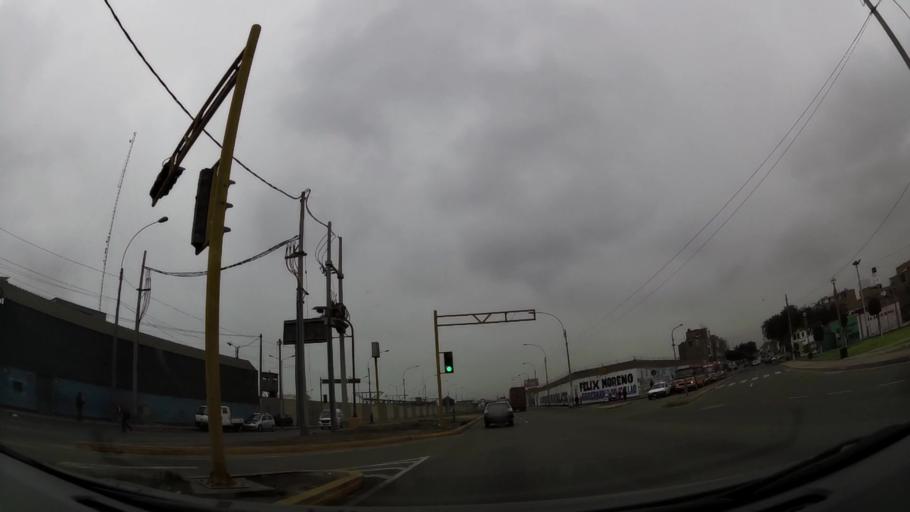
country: PE
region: Callao
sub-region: Callao
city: Callao
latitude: -12.0422
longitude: -77.1268
